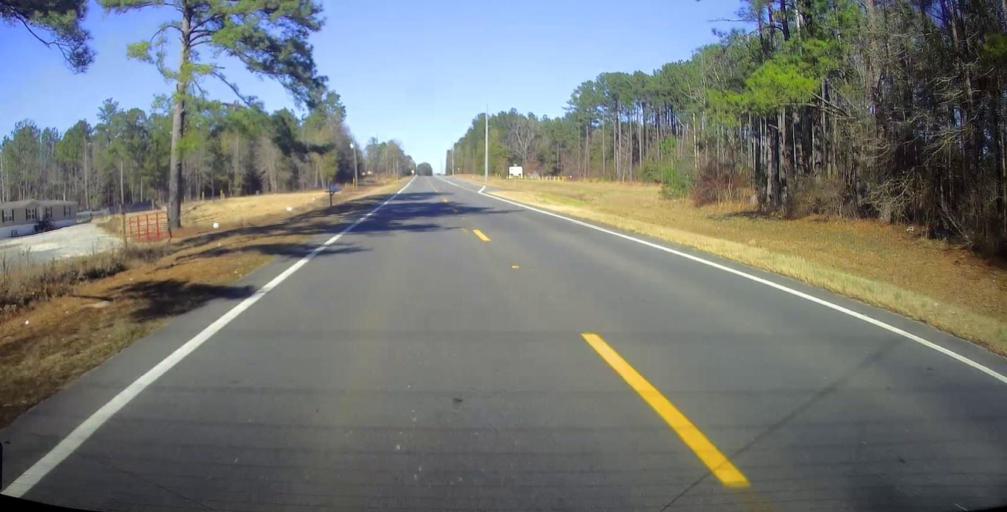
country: US
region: Georgia
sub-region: Macon County
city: Oglethorpe
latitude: 32.2276
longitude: -84.0989
